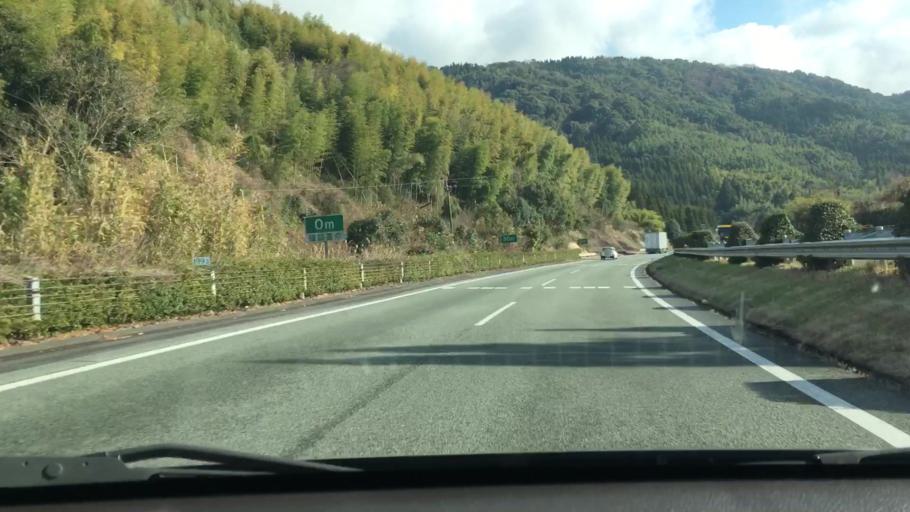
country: JP
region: Kumamoto
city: Matsubase
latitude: 32.6162
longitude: 130.7216
